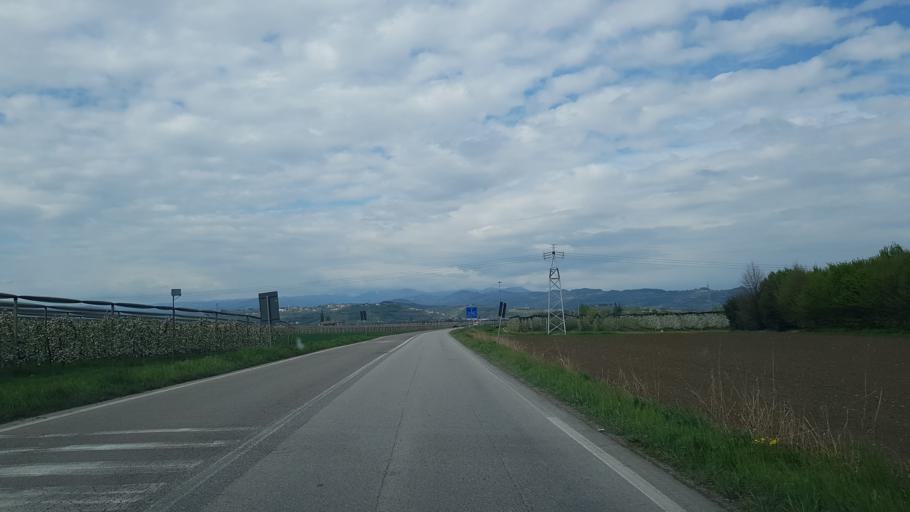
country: IT
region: Veneto
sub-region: Provincia di Verona
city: Belfiore
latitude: 45.3874
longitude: 11.2125
